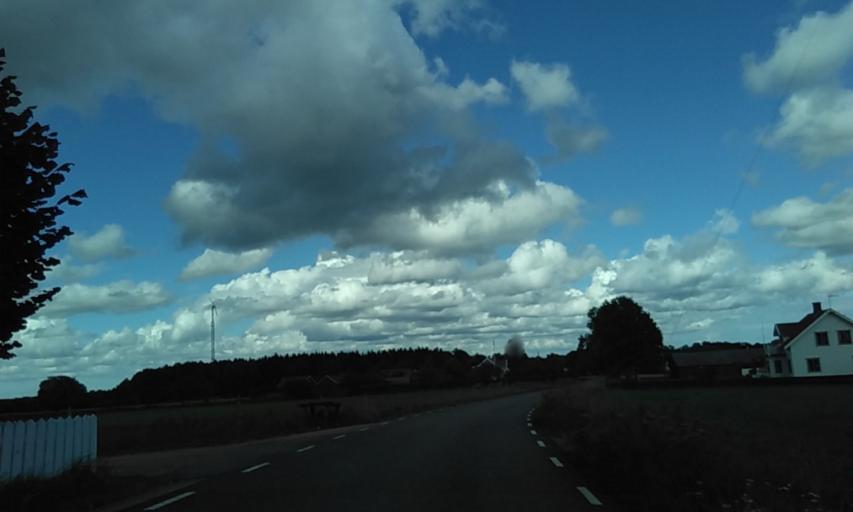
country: SE
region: Vaestra Goetaland
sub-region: Vargarda Kommun
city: Vargarda
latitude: 57.9824
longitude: 12.9173
